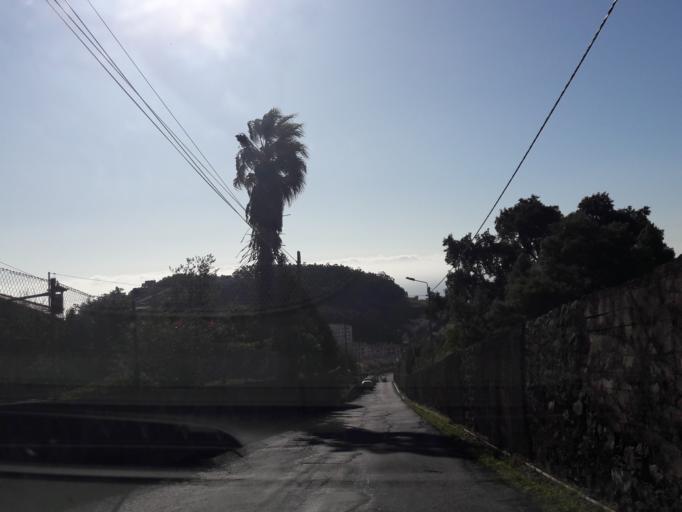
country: PT
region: Madeira
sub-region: Santa Cruz
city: Camacha
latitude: 32.6589
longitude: -16.8600
